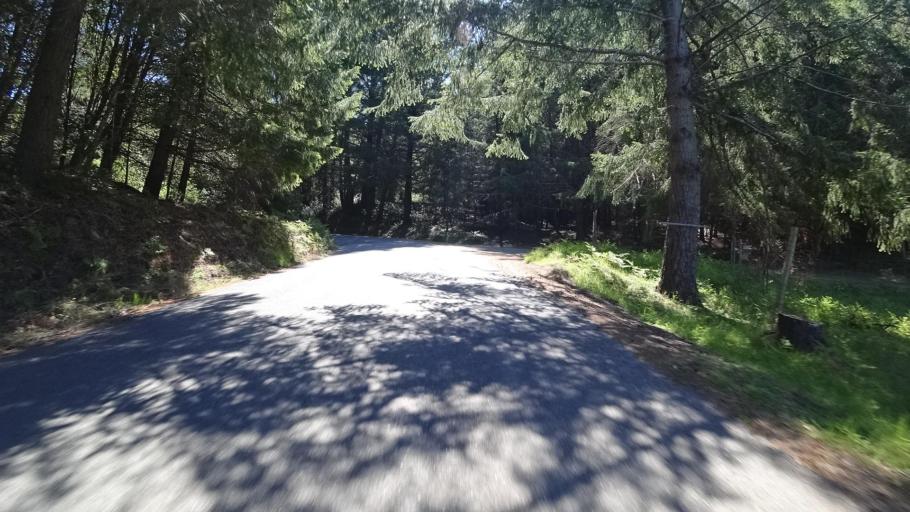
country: US
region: California
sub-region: Humboldt County
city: Redway
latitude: 40.1338
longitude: -123.9802
